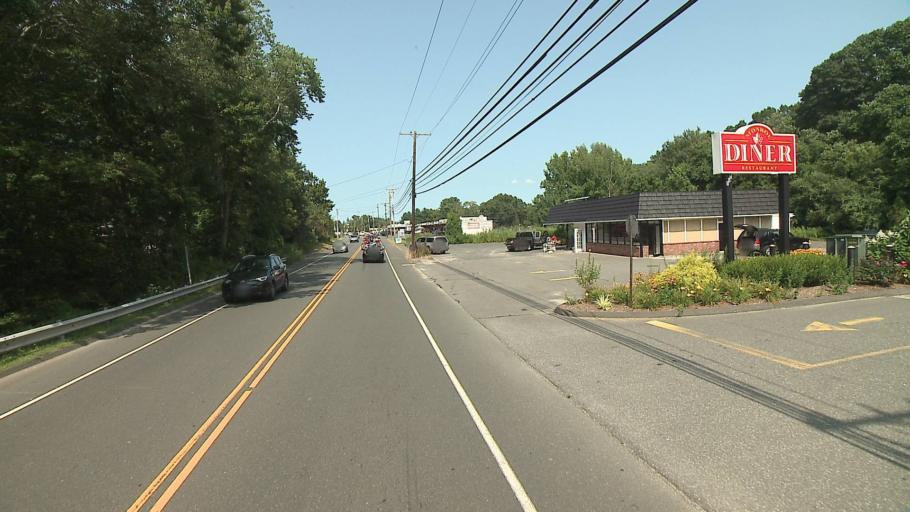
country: US
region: Connecticut
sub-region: Fairfield County
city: Newtown
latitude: 41.3308
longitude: -73.2654
